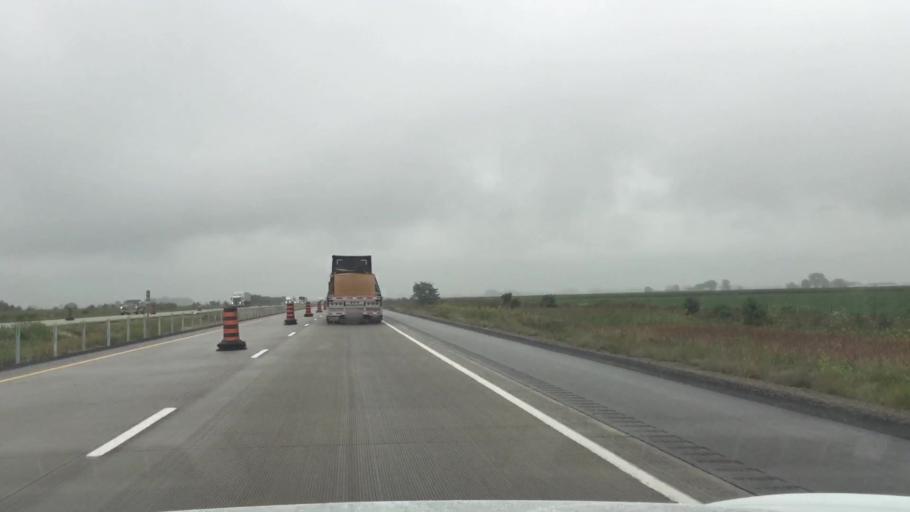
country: CA
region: Ontario
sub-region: Lambton County
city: Walpole Island
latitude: 42.3108
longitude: -82.3073
